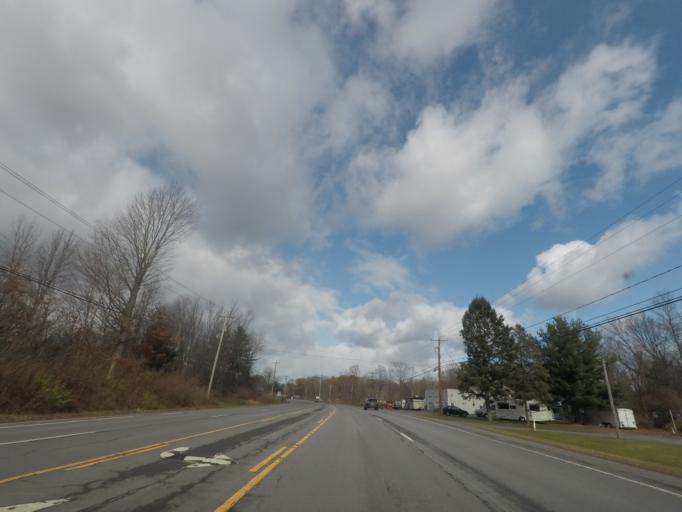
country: US
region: New York
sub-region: Saratoga County
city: Ballston Spa
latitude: 42.9837
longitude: -73.7867
